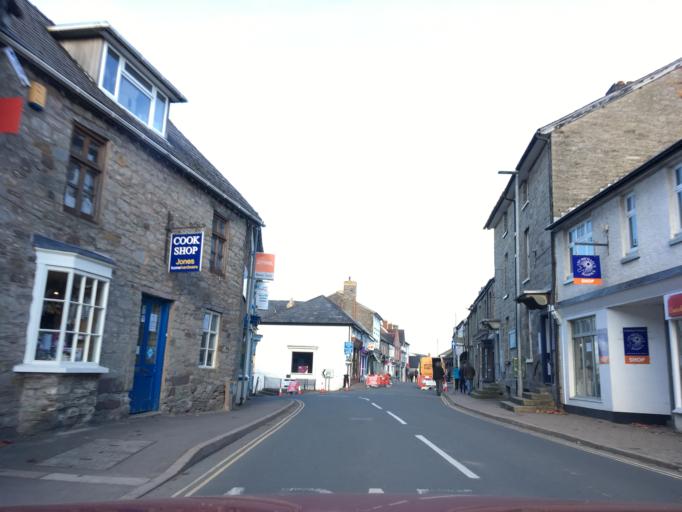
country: GB
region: Wales
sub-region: Sir Powys
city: Hay
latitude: 52.0734
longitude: -3.1278
